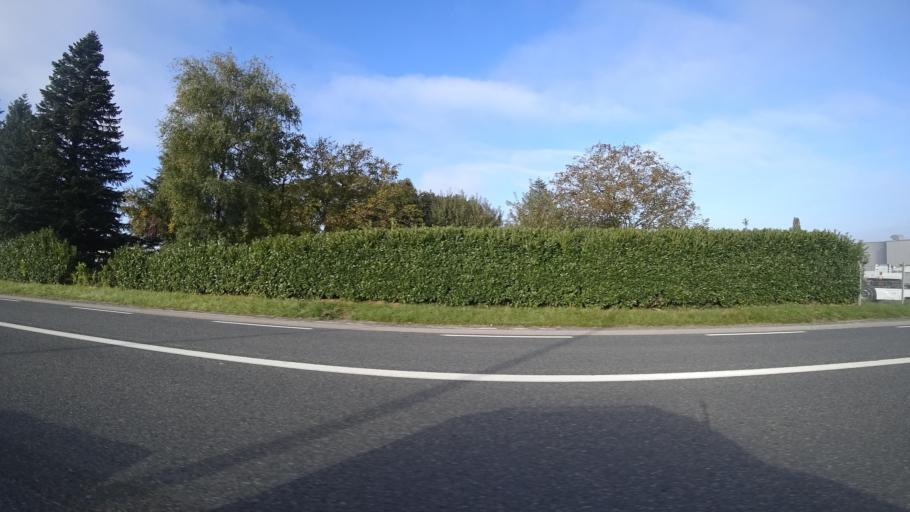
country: FR
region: Midi-Pyrenees
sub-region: Departement de l'Aveyron
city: Luc-la-Primaube
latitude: 44.3033
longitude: 2.5570
